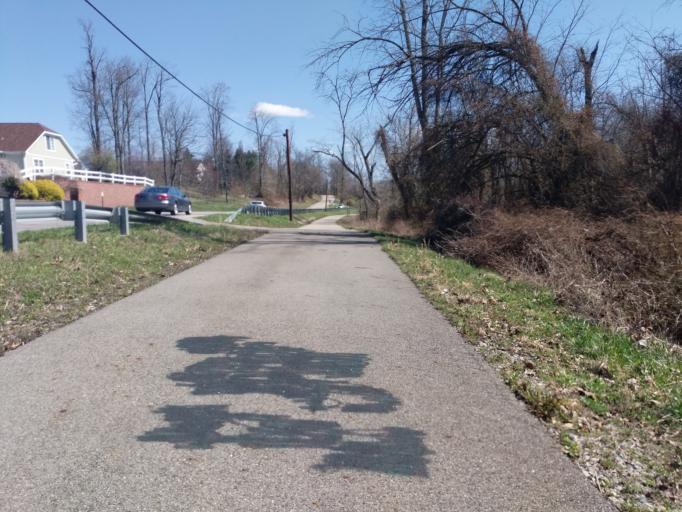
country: US
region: Ohio
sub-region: Athens County
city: The Plains
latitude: 39.3671
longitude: -82.1237
